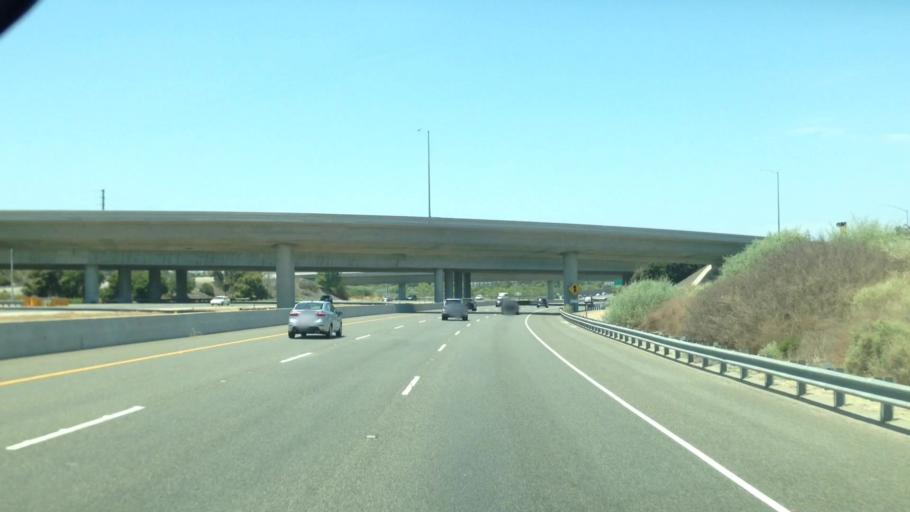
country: US
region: California
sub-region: Orange County
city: San Joaquin Hills
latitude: 33.6403
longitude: -117.8584
